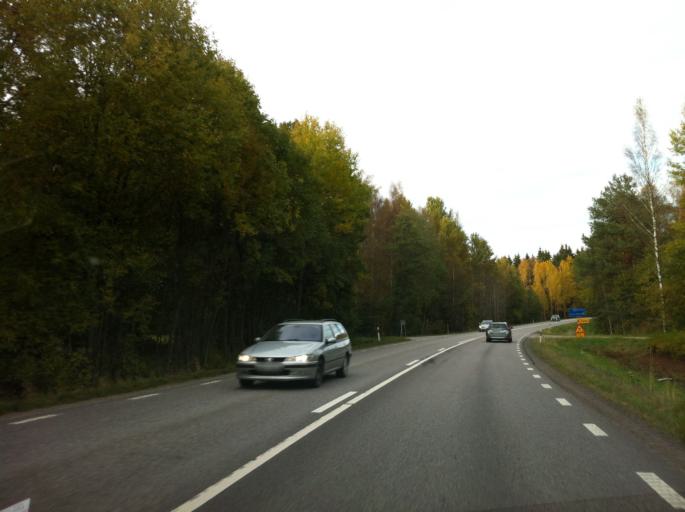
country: SE
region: OErebro
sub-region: Askersunds Kommun
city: Asbro
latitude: 58.9229
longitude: 14.9923
